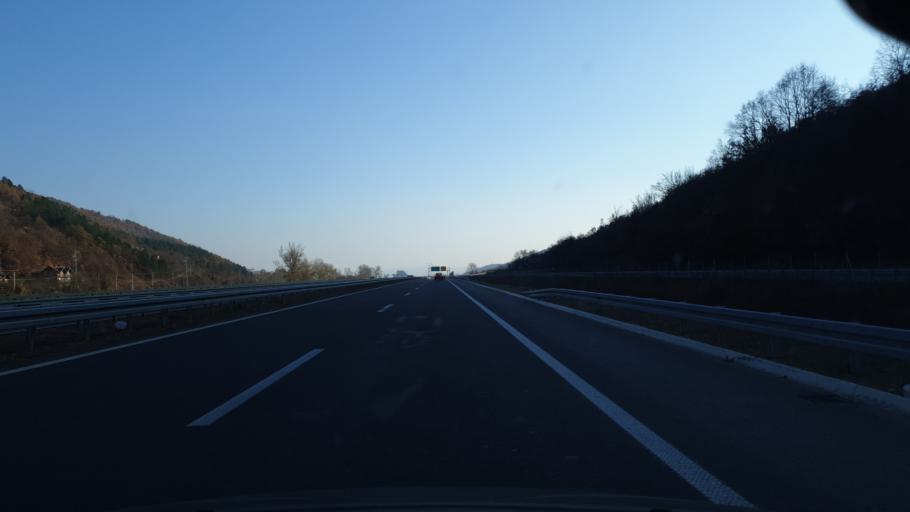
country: RS
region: Central Serbia
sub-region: Pirotski Okrug
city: Pirot
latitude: 43.1990
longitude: 22.5593
